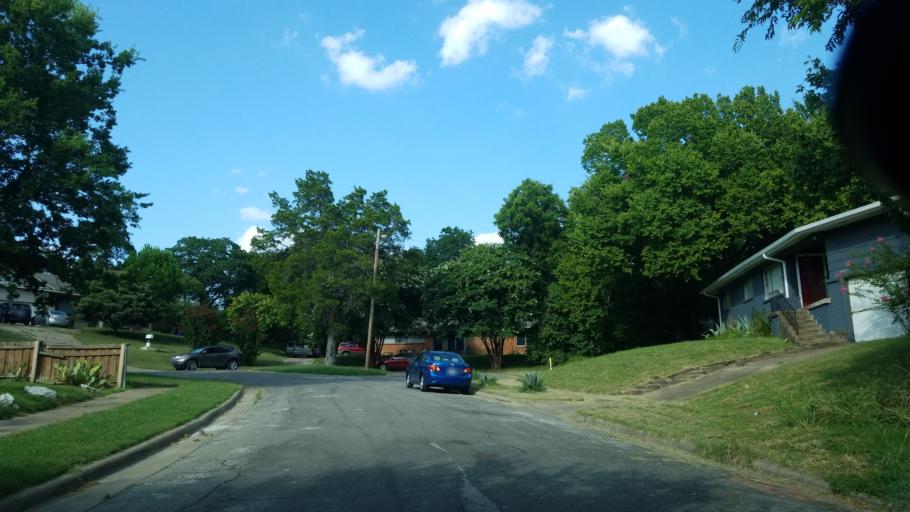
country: US
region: Texas
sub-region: Dallas County
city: Balch Springs
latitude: 32.7641
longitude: -96.7039
